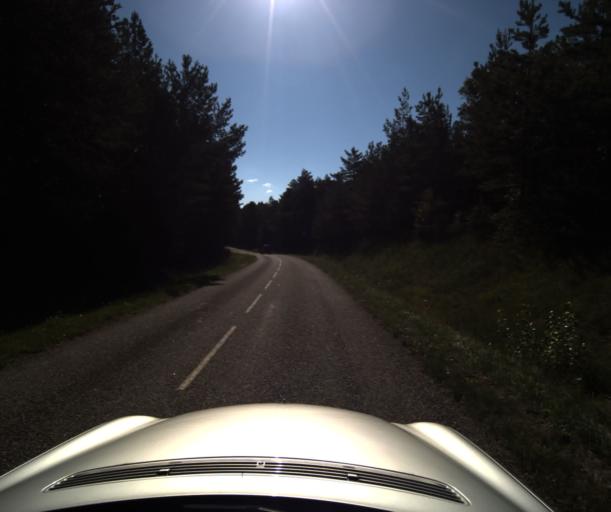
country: FR
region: Languedoc-Roussillon
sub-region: Departement de l'Aude
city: Chalabre
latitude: 42.9610
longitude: 1.9765
